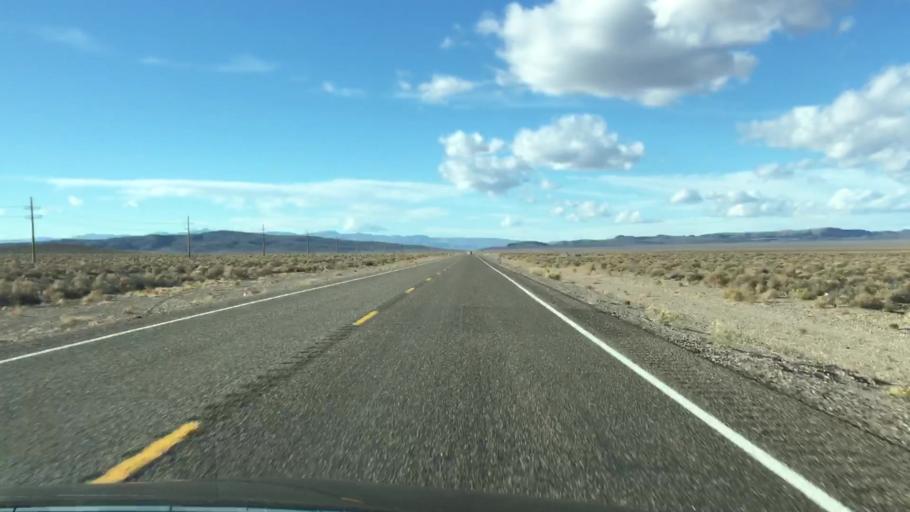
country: US
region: Nevada
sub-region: Nye County
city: Beatty
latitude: 37.1294
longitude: -116.8390
